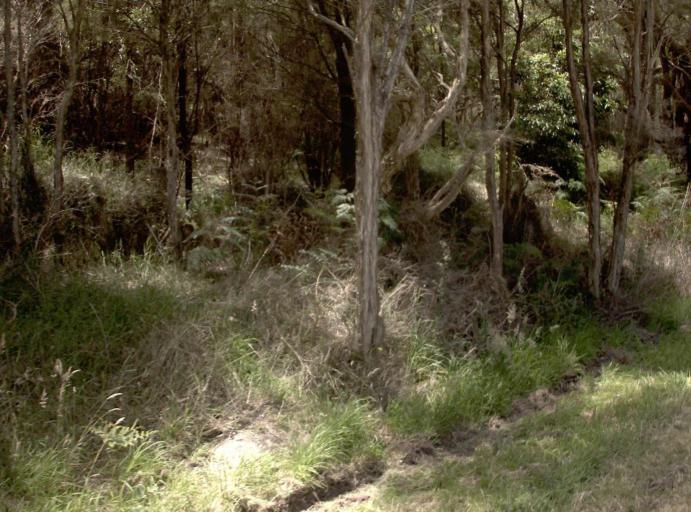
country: AU
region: Victoria
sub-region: Bass Coast
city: North Wonthaggi
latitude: -38.7314
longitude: 146.1233
